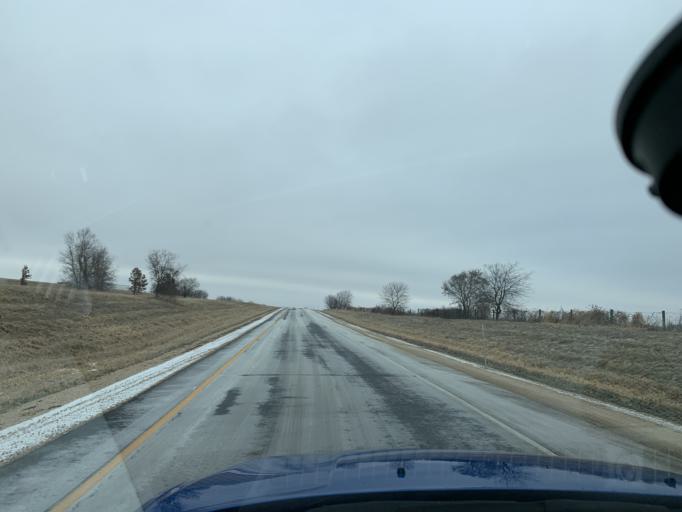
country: US
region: Wisconsin
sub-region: Dane County
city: Sun Prairie
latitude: 43.2396
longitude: -89.1457
